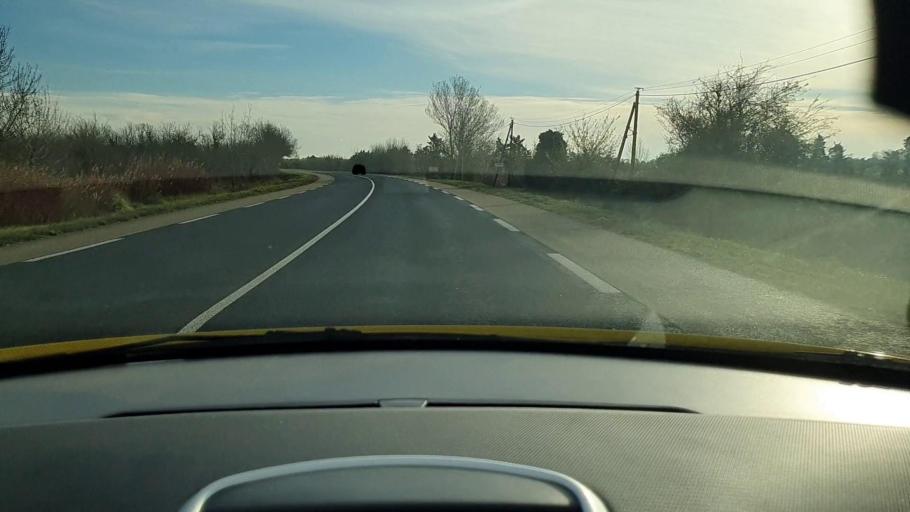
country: FR
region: Languedoc-Roussillon
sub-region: Departement du Gard
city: Fourques
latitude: 43.6950
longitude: 4.5899
